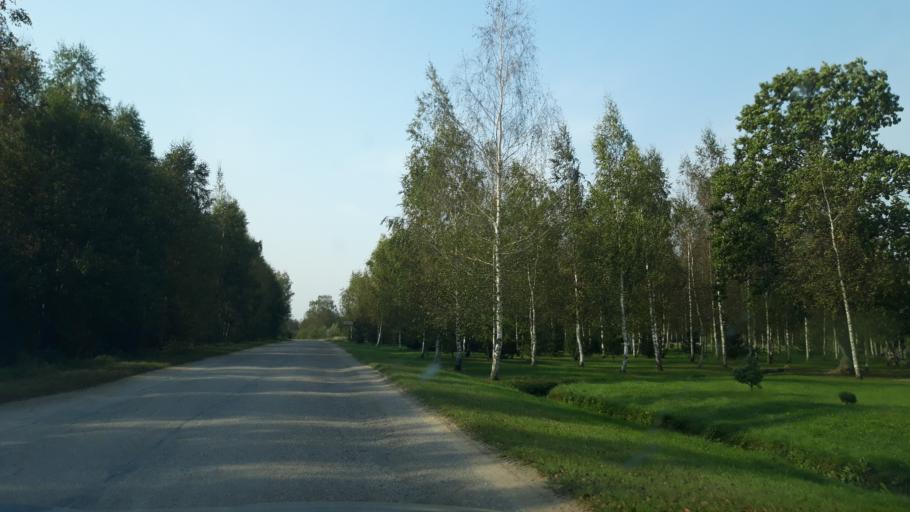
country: LV
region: Mazsalaca
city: Mazsalaca
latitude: 57.8528
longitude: 25.0404
